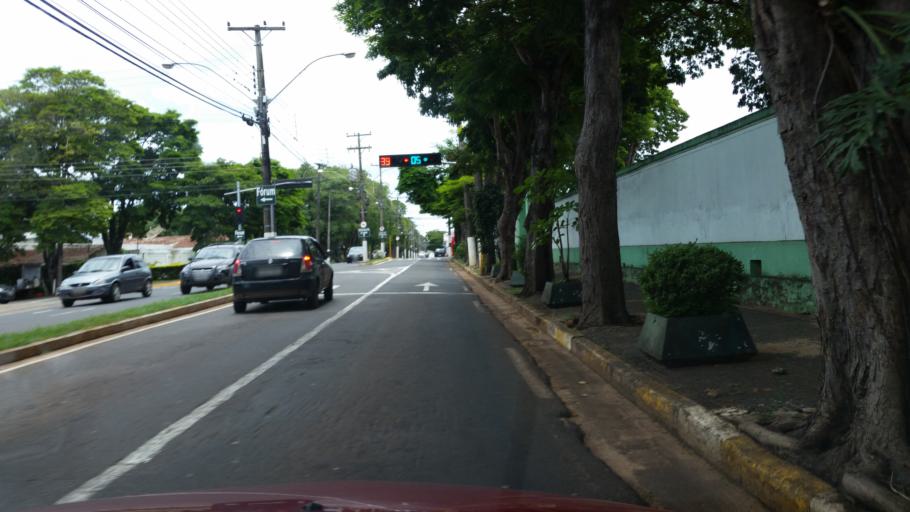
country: BR
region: Sao Paulo
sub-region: Avare
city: Avare
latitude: -23.0969
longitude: -48.9352
